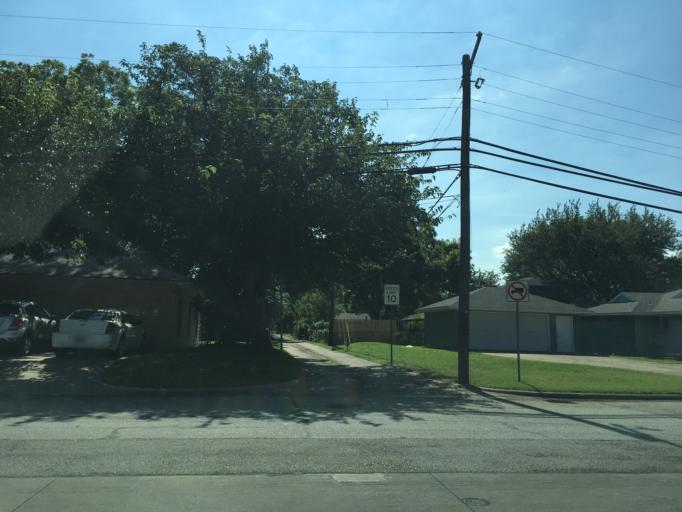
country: US
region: Texas
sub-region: Dallas County
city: Farmers Branch
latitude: 32.9232
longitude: -96.8793
